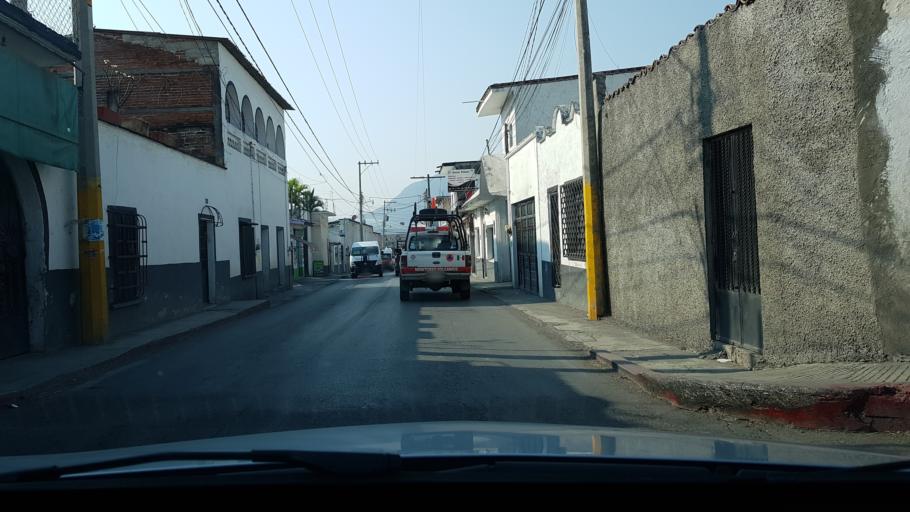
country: MX
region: Morelos
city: Tlaquiltenango
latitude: 18.6315
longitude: -99.1621
